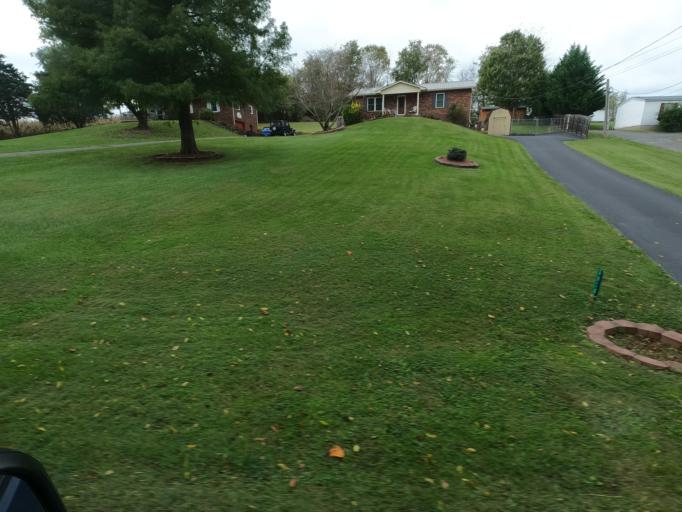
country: US
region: Tennessee
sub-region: Washington County
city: Jonesborough
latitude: 36.2393
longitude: -82.5568
